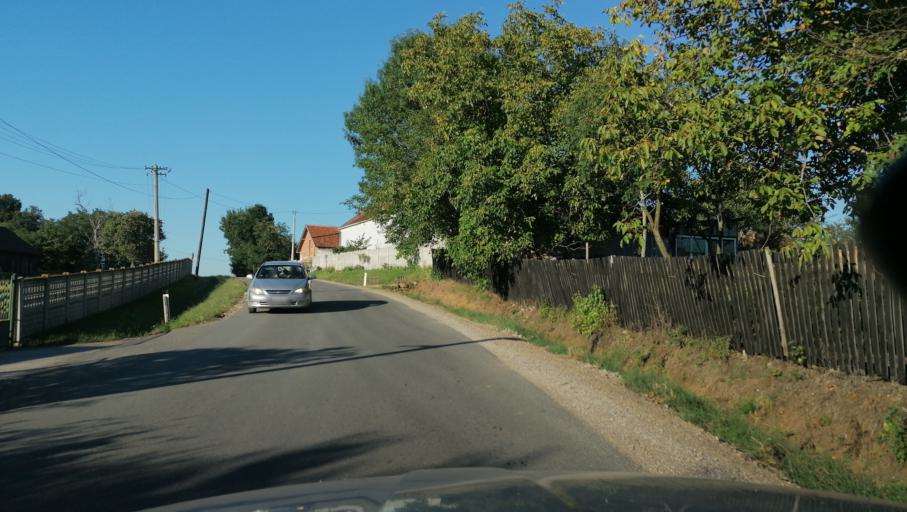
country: RS
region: Central Serbia
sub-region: Sumadijski Okrug
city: Kragujevac
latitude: 44.1116
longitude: 20.8356
